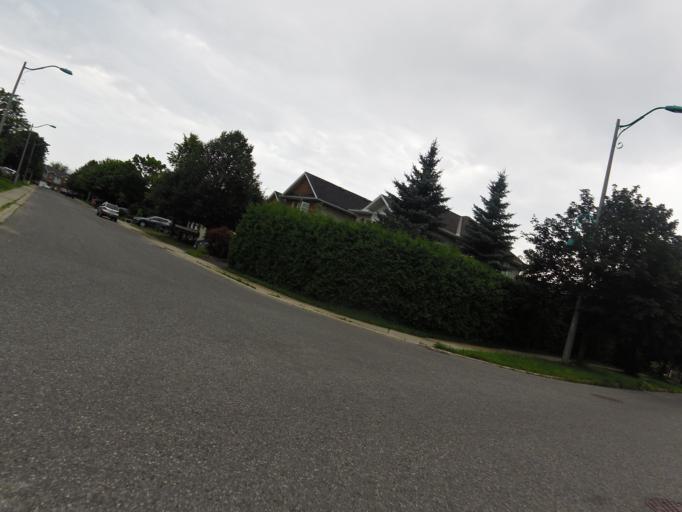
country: CA
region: Ontario
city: Bells Corners
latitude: 45.3203
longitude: -75.8934
